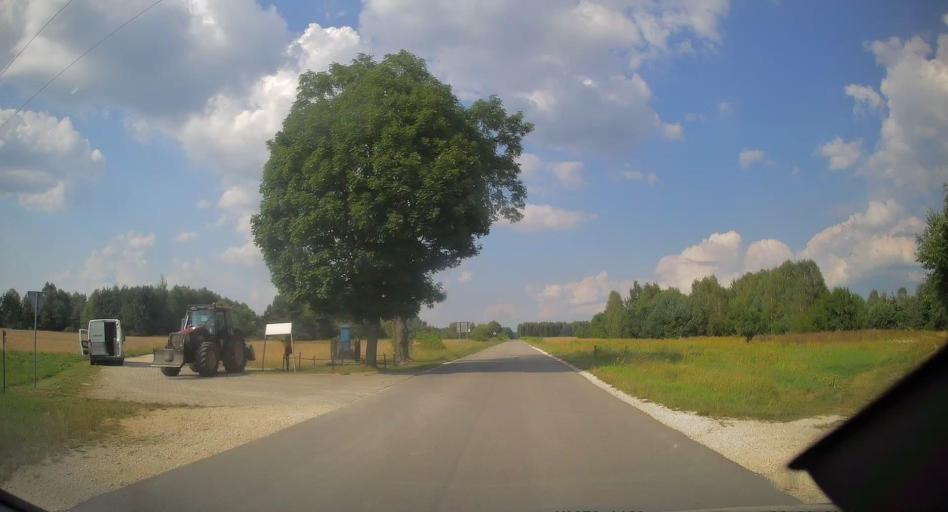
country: PL
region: Swietokrzyskie
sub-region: Powiat konecki
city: Radoszyce
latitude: 51.0900
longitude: 20.2592
